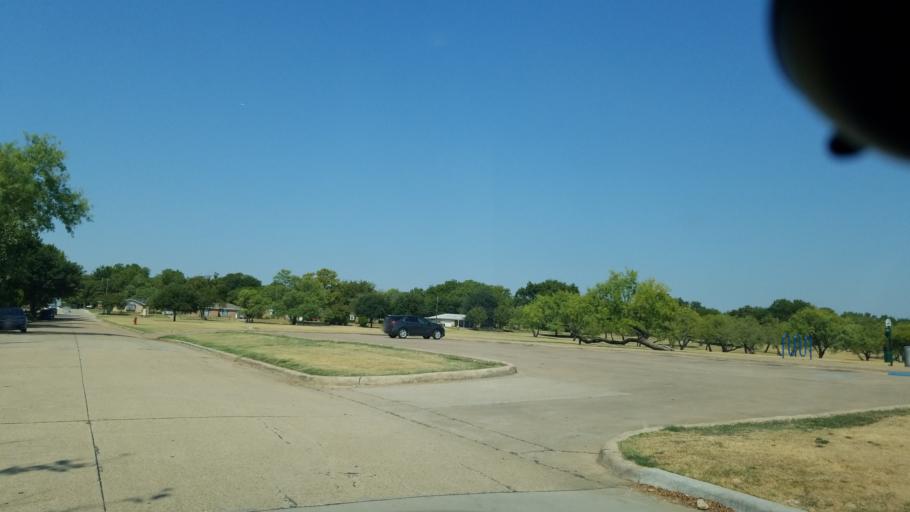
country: US
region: Texas
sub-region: Dallas County
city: Grand Prairie
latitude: 32.7104
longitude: -96.9791
